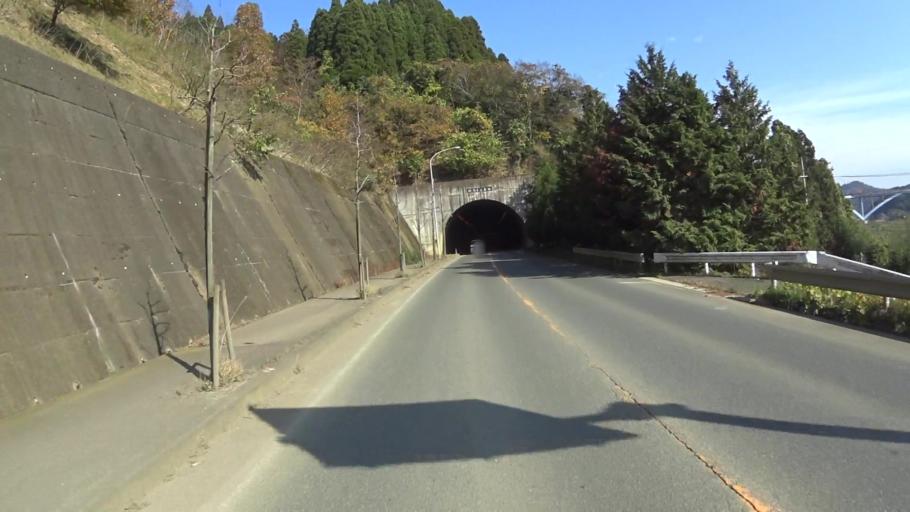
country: JP
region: Kyoto
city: Miyazu
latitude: 35.4211
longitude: 135.2050
